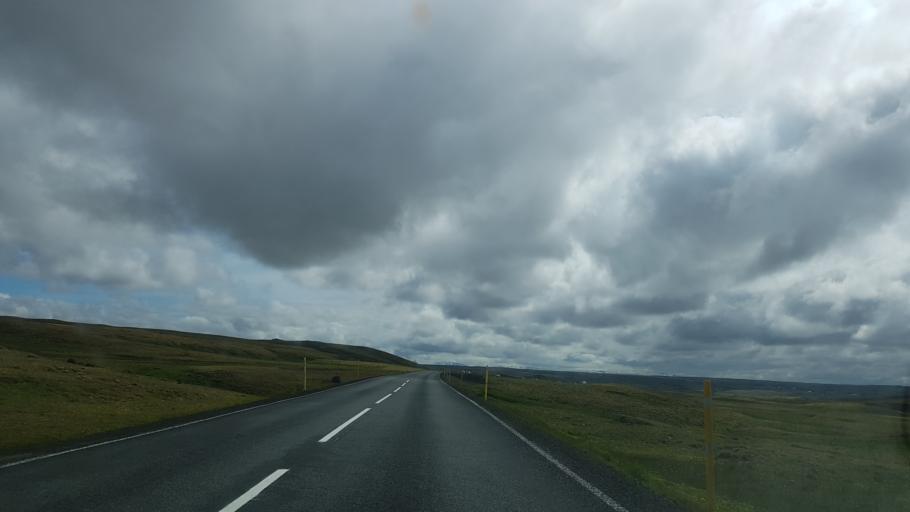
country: IS
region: West
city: Borgarnes
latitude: 64.9669
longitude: -21.0650
